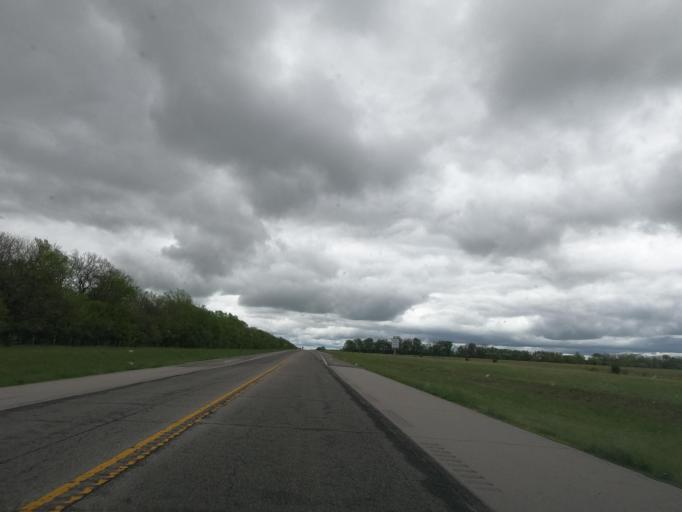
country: US
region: Kansas
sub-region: Montgomery County
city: Cherryvale
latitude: 37.3469
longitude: -95.5166
